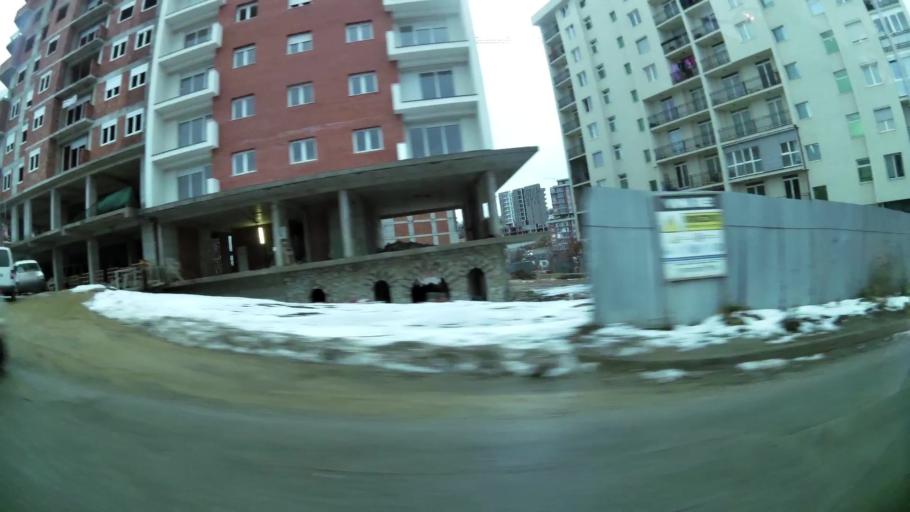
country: XK
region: Pristina
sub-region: Komuna e Prishtines
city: Pristina
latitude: 42.6388
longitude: 21.1638
